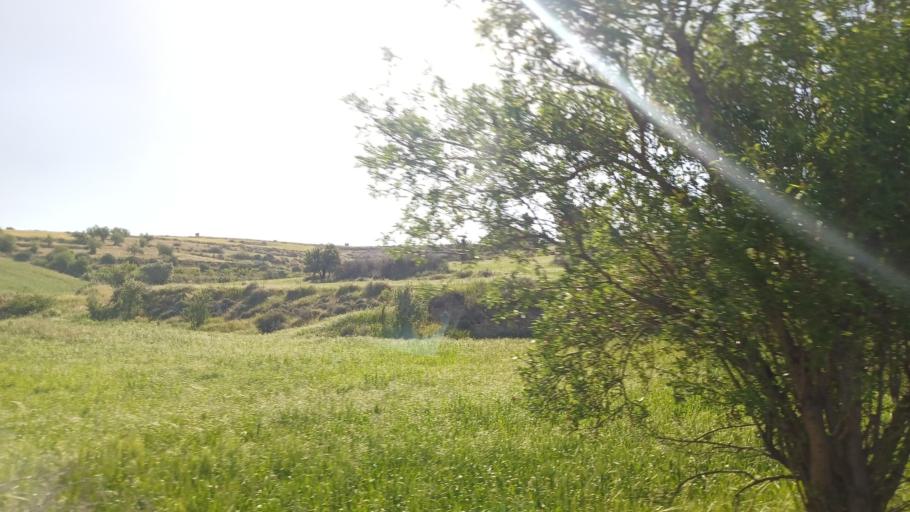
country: CY
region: Lefkosia
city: Astromeritis
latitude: 35.0837
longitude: 33.0188
